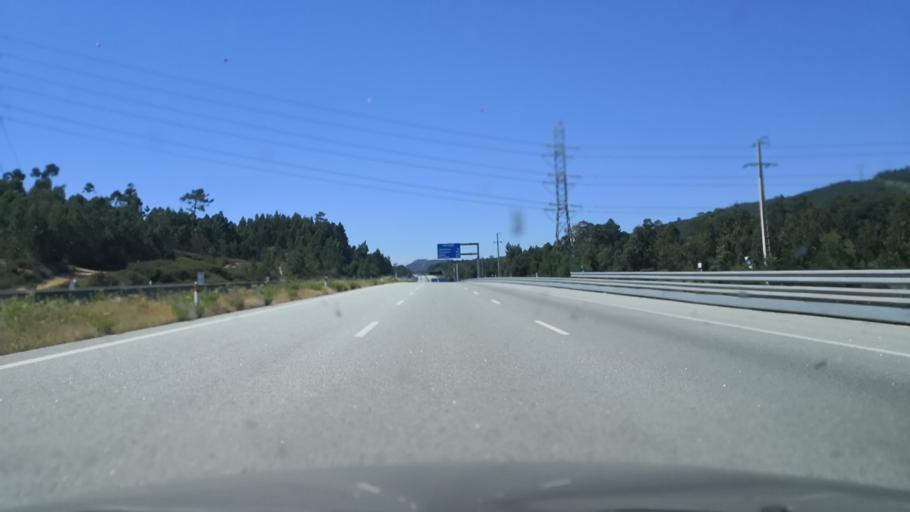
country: PT
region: Porto
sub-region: Gondomar
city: Foz do Sousa
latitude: 41.0751
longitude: -8.4521
